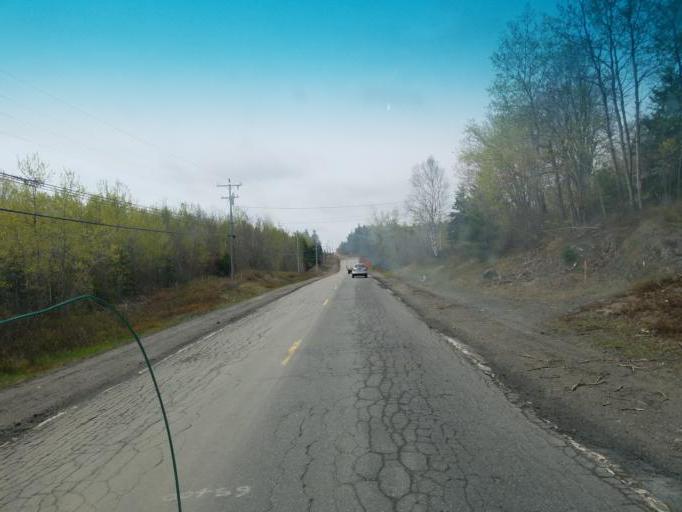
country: US
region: Maine
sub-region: Washington County
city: East Machias
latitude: 44.7774
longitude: -67.1957
